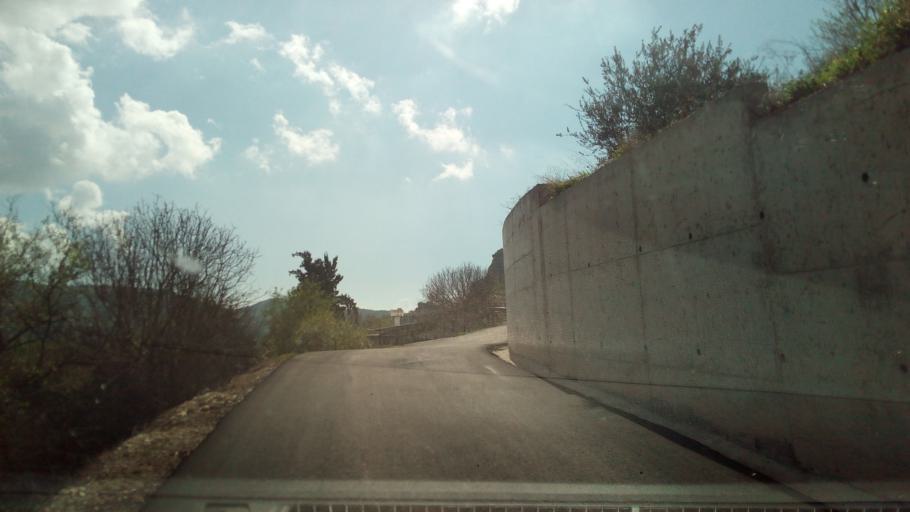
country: CY
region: Pafos
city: Mesogi
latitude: 34.7994
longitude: 32.5266
